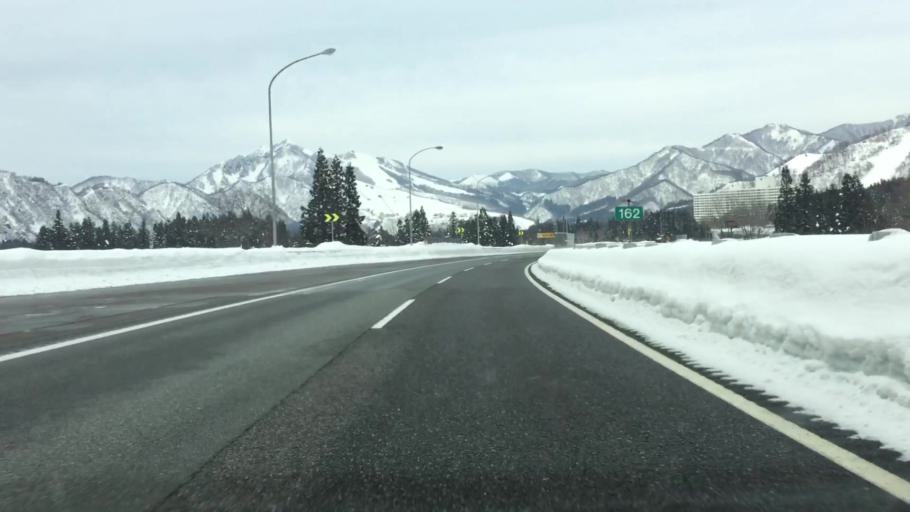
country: JP
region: Niigata
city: Shiozawa
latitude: 36.8959
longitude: 138.8452
